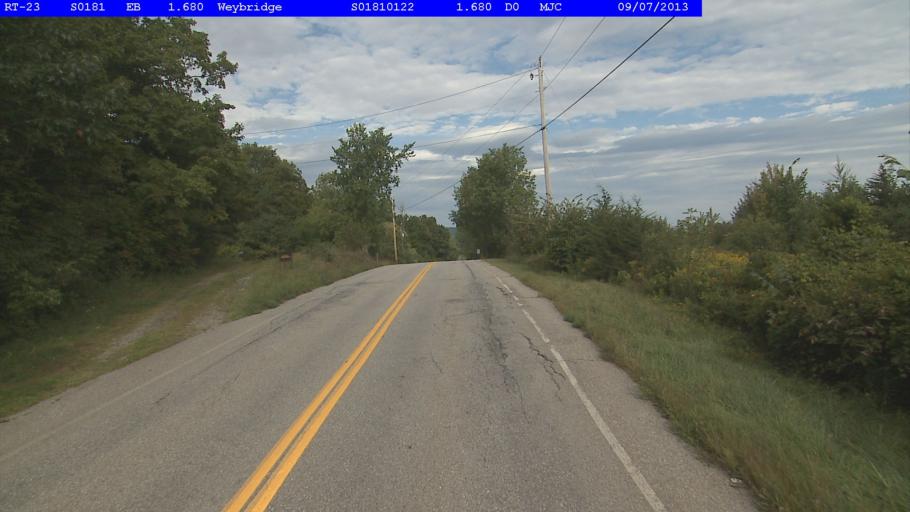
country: US
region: Vermont
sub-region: Addison County
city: Middlebury (village)
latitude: 44.0354
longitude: -73.2066
